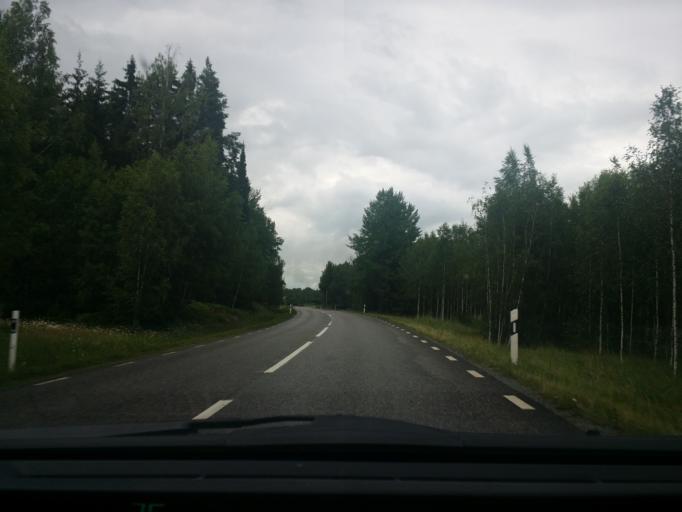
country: SE
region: OErebro
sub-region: Lindesbergs Kommun
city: Frovi
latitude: 59.4541
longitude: 15.3182
